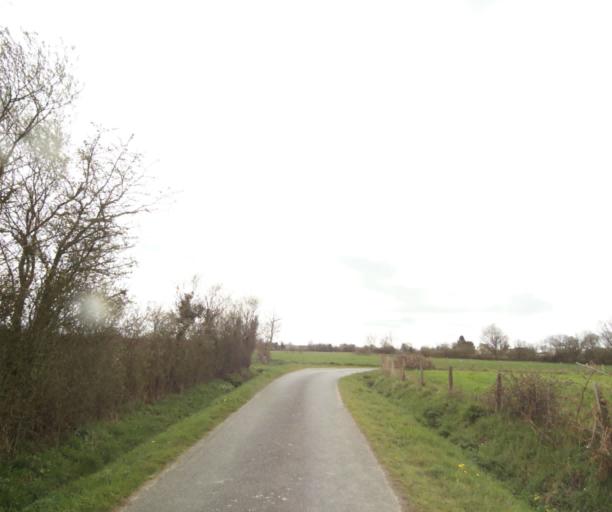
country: FR
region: Pays de la Loire
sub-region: Departement de la Loire-Atlantique
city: Bouvron
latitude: 47.4283
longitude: -1.8604
